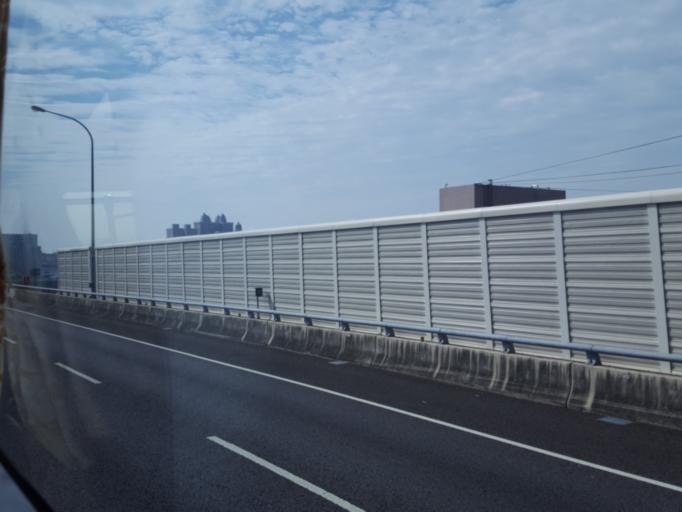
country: TW
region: Taiwan
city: Taoyuan City
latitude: 25.0431
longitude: 121.3066
